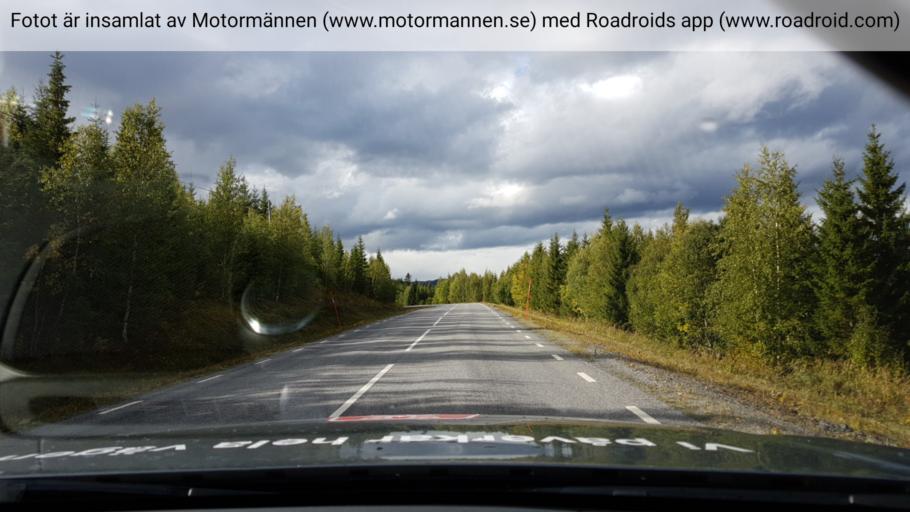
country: SE
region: Jaemtland
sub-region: Are Kommun
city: Are
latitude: 63.5877
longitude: 13.0700
